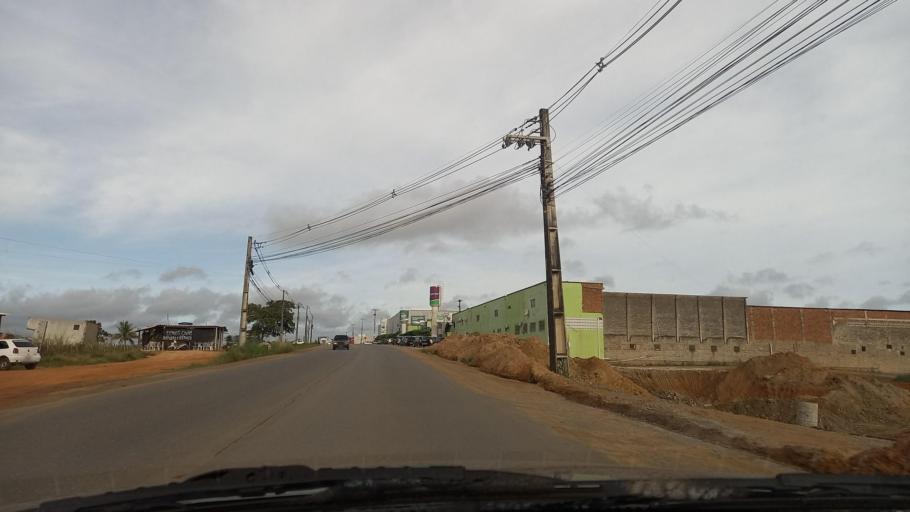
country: BR
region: Pernambuco
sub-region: Vitoria De Santo Antao
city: Vitoria de Santo Antao
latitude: -8.1216
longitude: -35.3308
